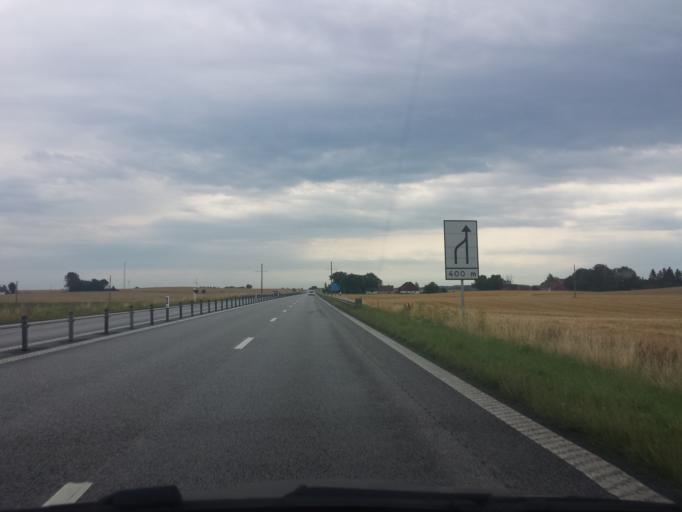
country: SE
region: Skane
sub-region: Skurups Kommun
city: Rydsgard
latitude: 55.4802
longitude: 13.6206
